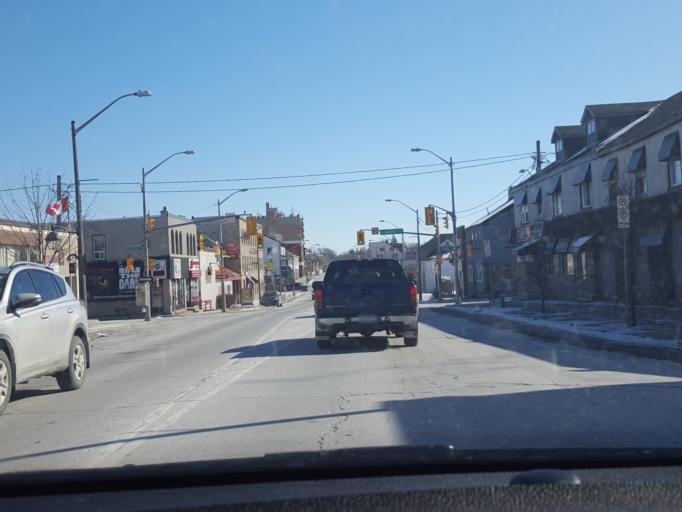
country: CA
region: Ontario
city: Cambridge
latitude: 43.3948
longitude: -80.3563
